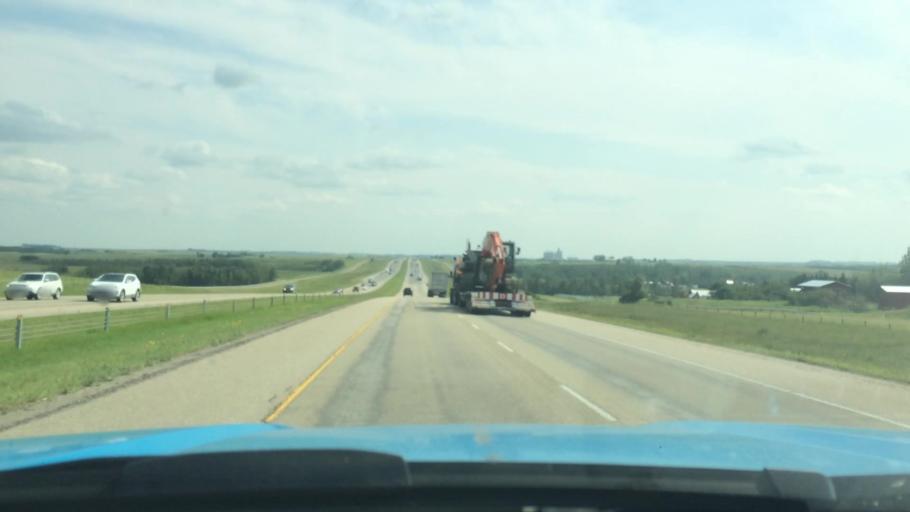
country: CA
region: Alberta
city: Carstairs
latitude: 51.5230
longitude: -114.0253
